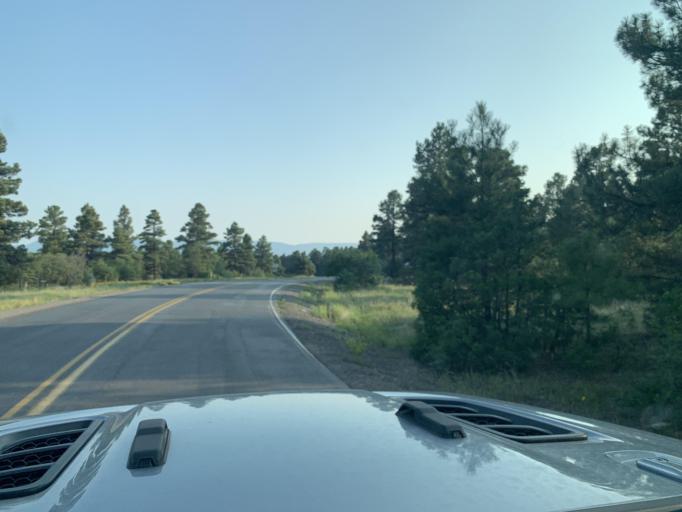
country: US
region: Colorado
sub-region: Archuleta County
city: Pagosa Springs
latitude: 37.2767
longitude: -107.0966
